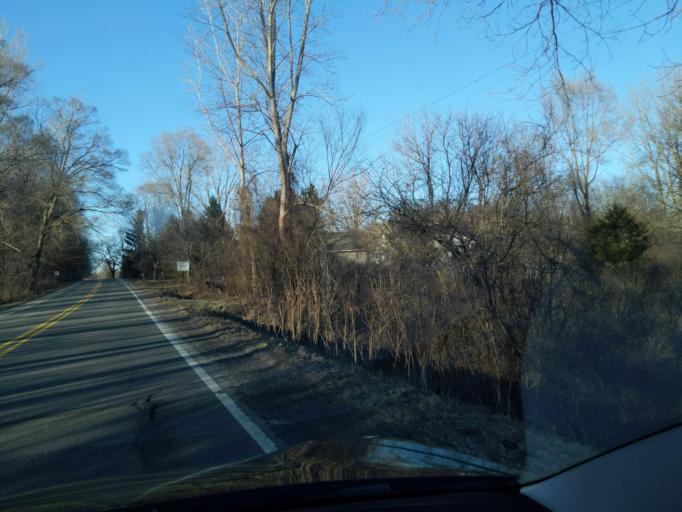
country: US
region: Michigan
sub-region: Washtenaw County
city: Chelsea
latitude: 42.3390
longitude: -84.0276
